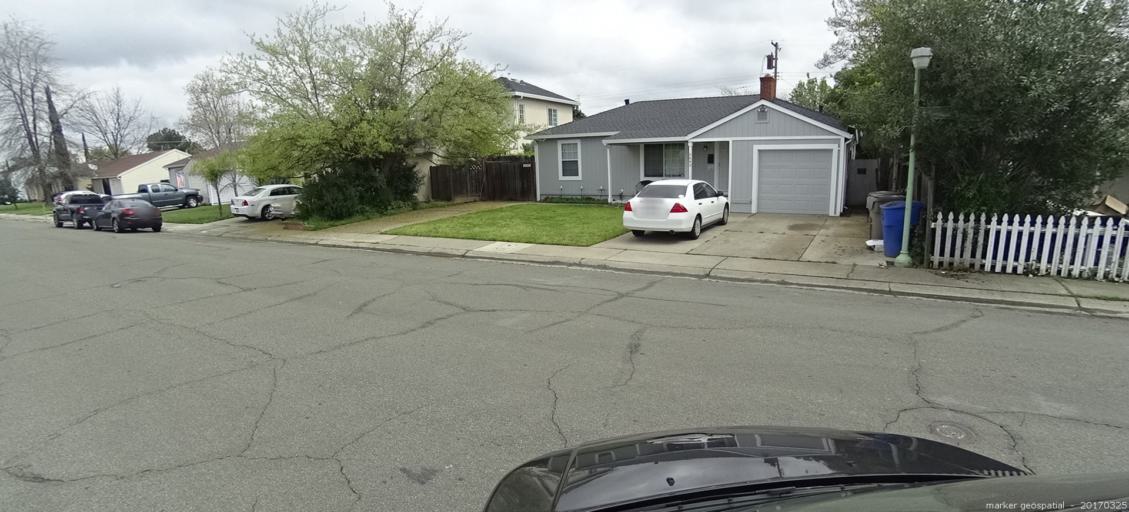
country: US
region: California
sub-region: Sacramento County
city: Parkway
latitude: 38.5236
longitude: -121.4338
